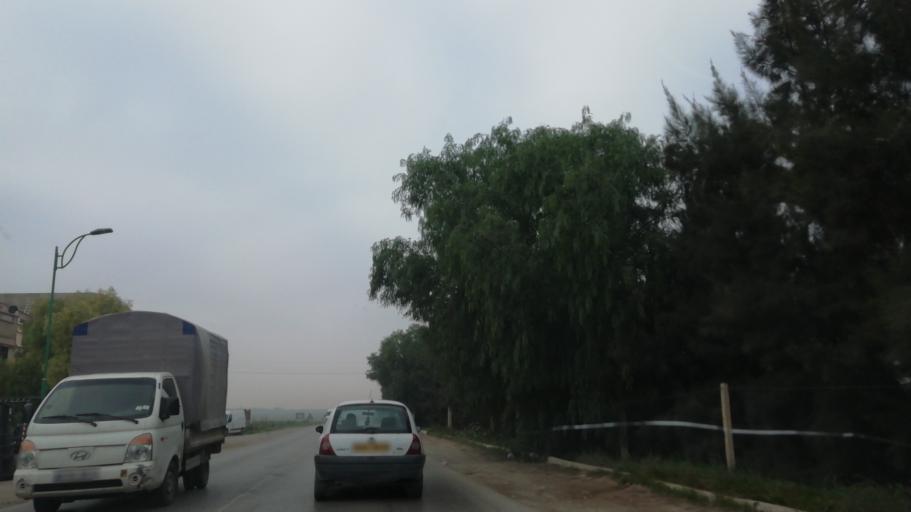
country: DZ
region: Relizane
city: Djidiouia
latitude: 35.9038
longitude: 0.7705
